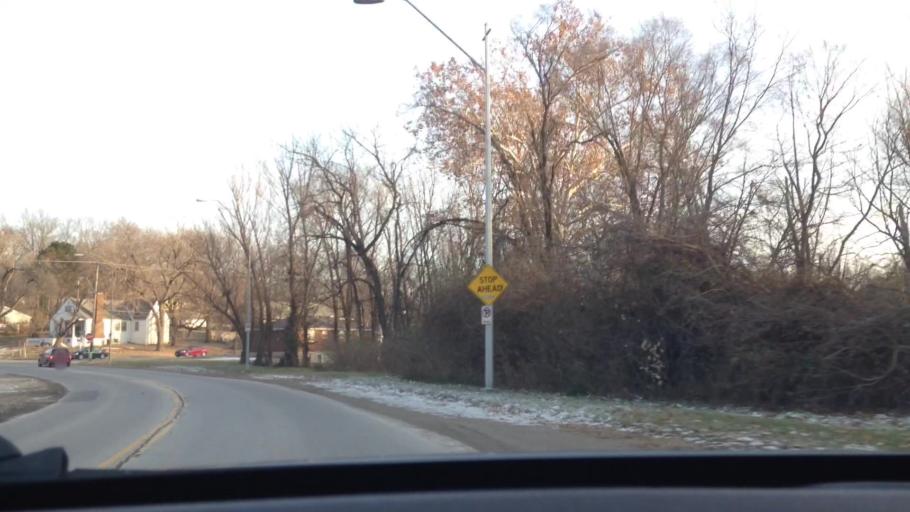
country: US
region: Missouri
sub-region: Clay County
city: North Kansas City
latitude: 39.1635
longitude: -94.5483
